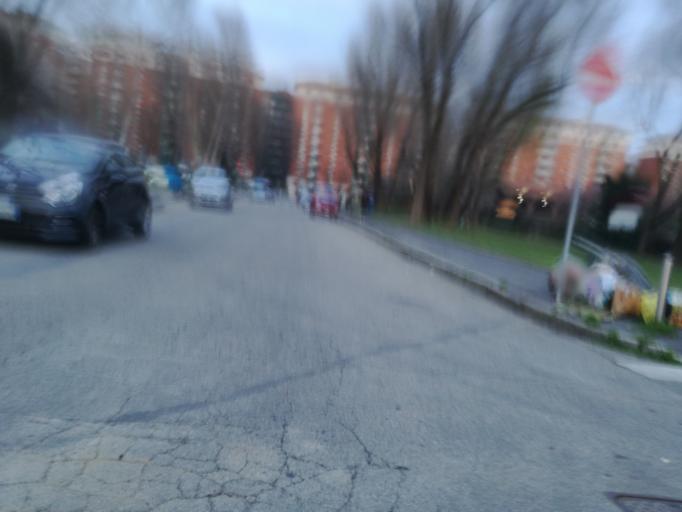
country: IT
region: Lombardy
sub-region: Citta metropolitana di Milano
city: Romano Banco
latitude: 45.4525
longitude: 9.1321
